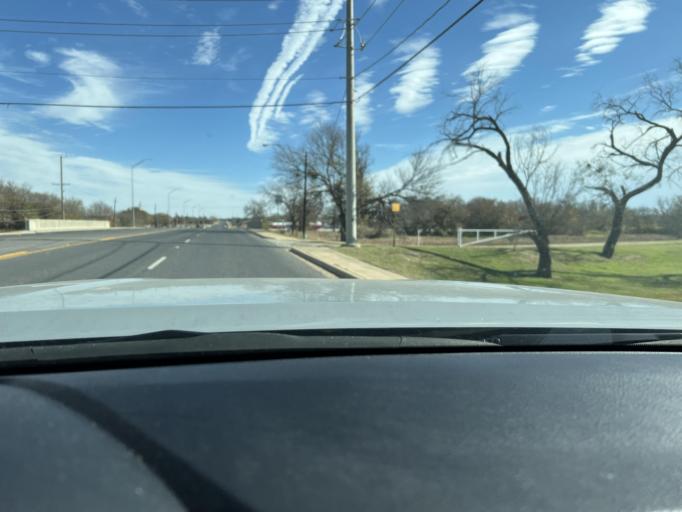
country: US
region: Texas
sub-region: Eastland County
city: Eastland
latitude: 32.4017
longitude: -98.8117
